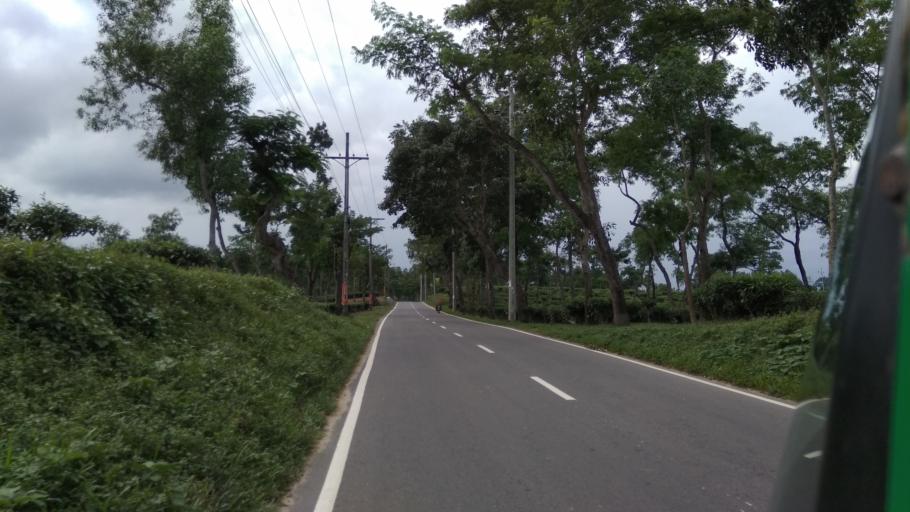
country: IN
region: Tripura
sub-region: Dhalai
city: Kamalpur
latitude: 24.3016
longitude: 91.7517
